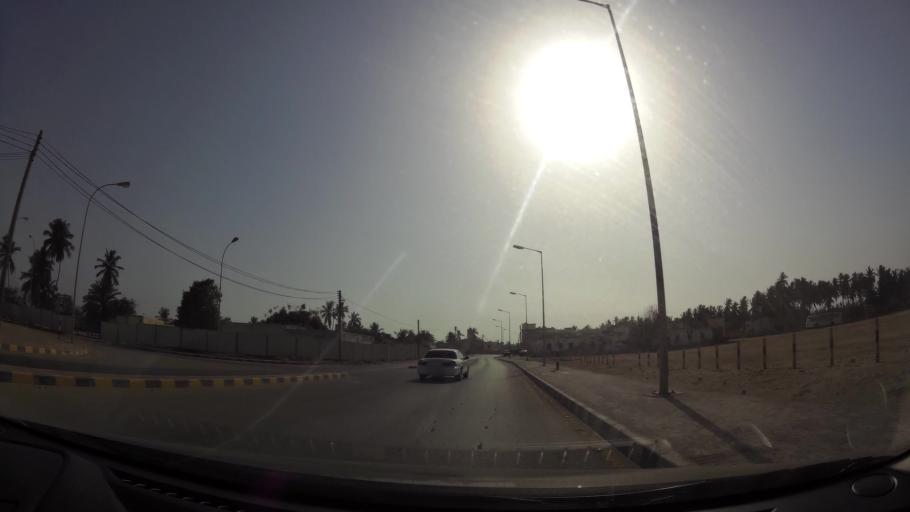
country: OM
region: Zufar
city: Salalah
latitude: 17.0030
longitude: 54.1113
